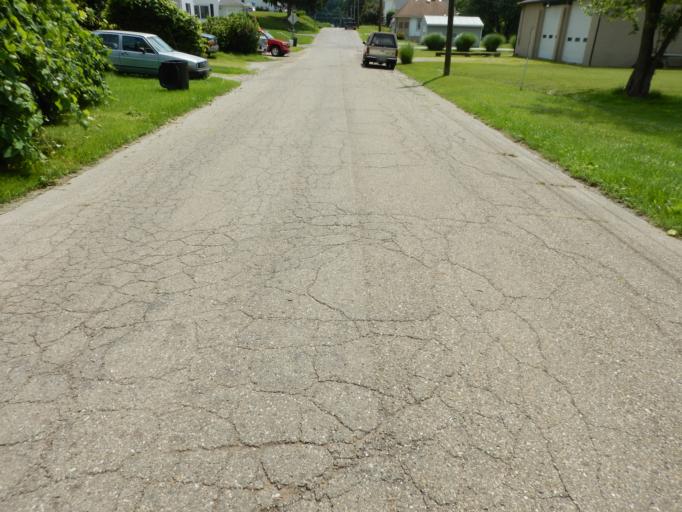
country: US
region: Ohio
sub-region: Muskingum County
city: South Zanesville
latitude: 39.9132
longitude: -82.0195
